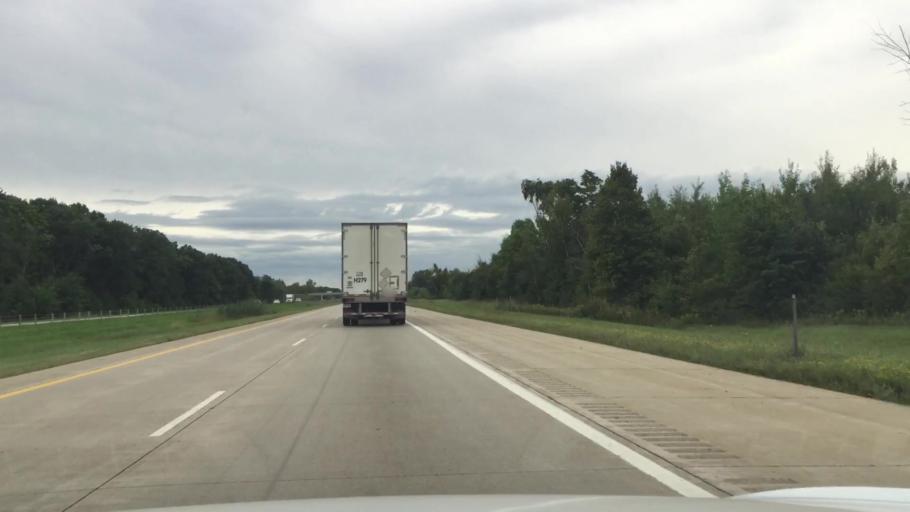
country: US
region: Michigan
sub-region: Saint Clair County
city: Marysville
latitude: 42.9424
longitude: -82.5078
